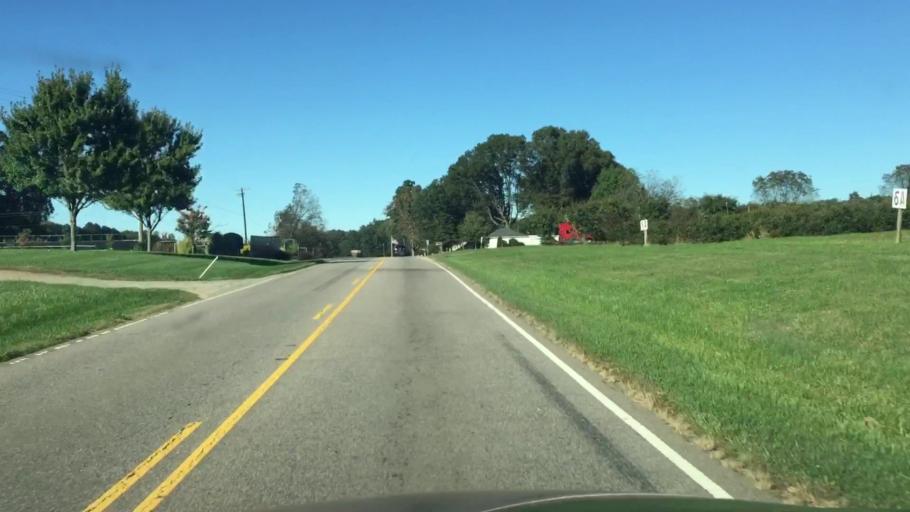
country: US
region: North Carolina
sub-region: Gaston County
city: Davidson
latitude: 35.5041
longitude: -80.7686
